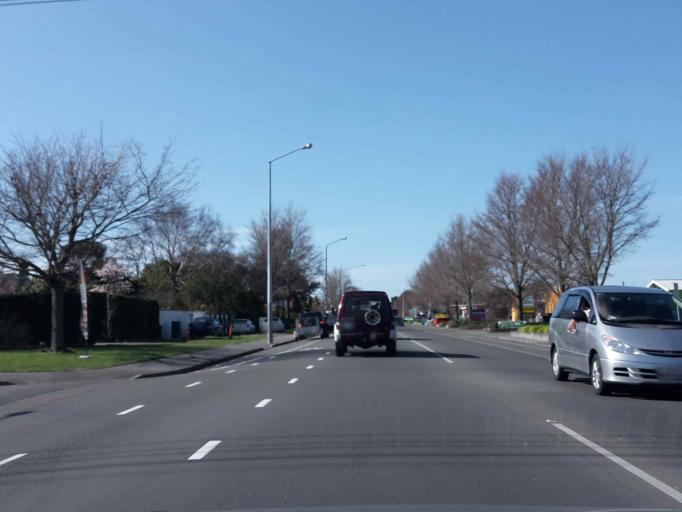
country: NZ
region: Canterbury
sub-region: Selwyn District
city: Prebbleton
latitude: -43.5377
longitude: 172.5567
